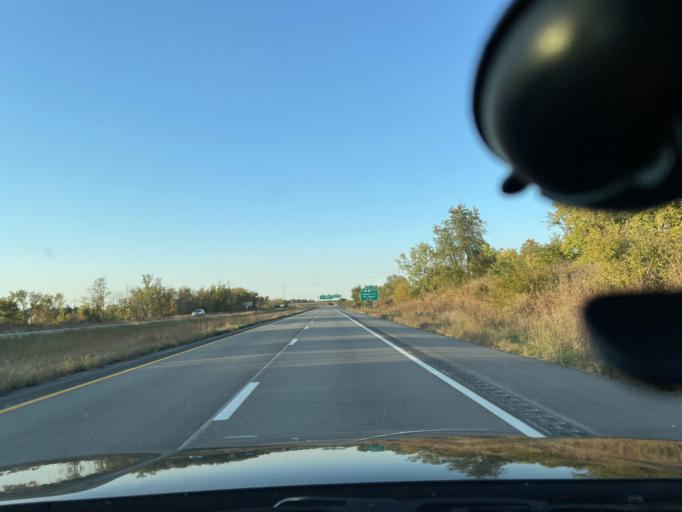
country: US
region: Missouri
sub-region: Andrew County
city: Country Club Village
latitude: 39.8749
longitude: -94.8571
